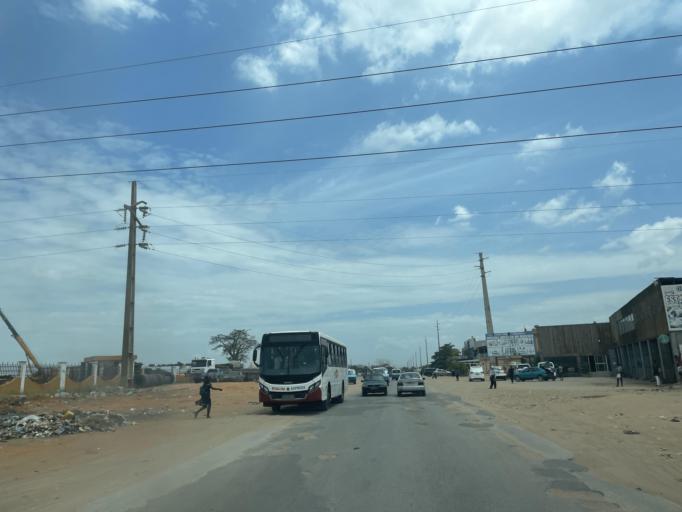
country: AO
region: Luanda
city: Luanda
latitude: -8.9367
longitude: 13.3824
